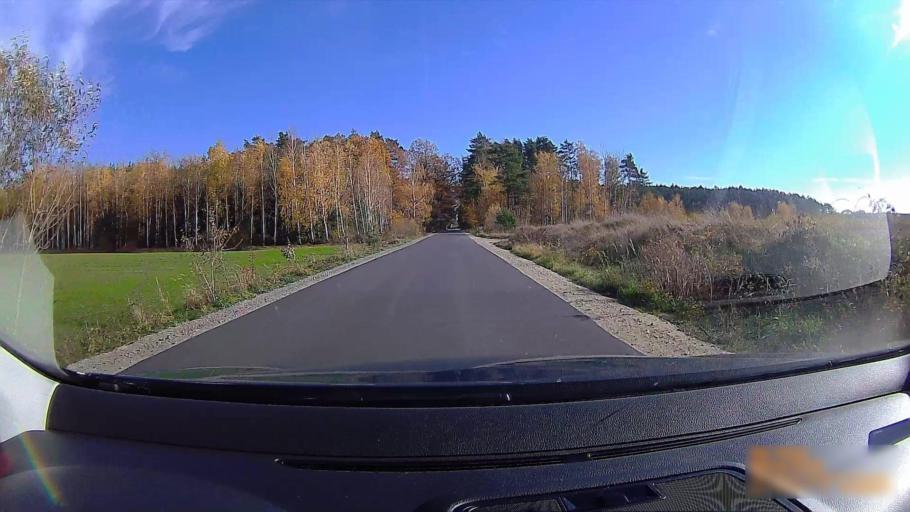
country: PL
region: Greater Poland Voivodeship
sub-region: Powiat ostrzeszowski
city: Doruchow
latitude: 51.4057
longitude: 18.0139
